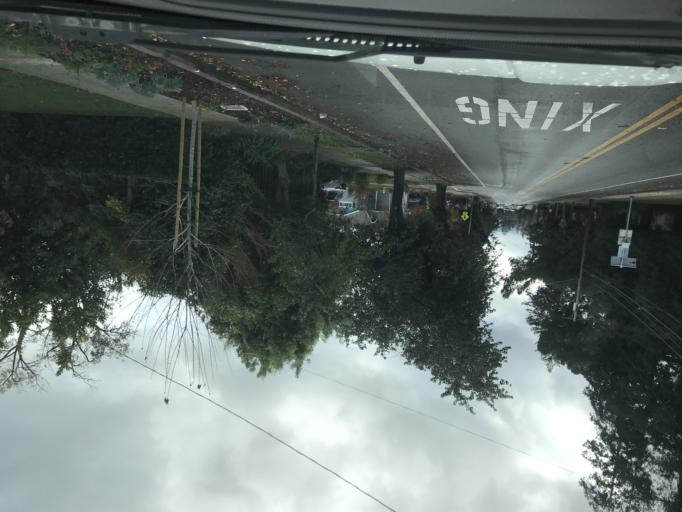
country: US
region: California
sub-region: Santa Clara County
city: Buena Vista
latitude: 37.2977
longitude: -121.9054
